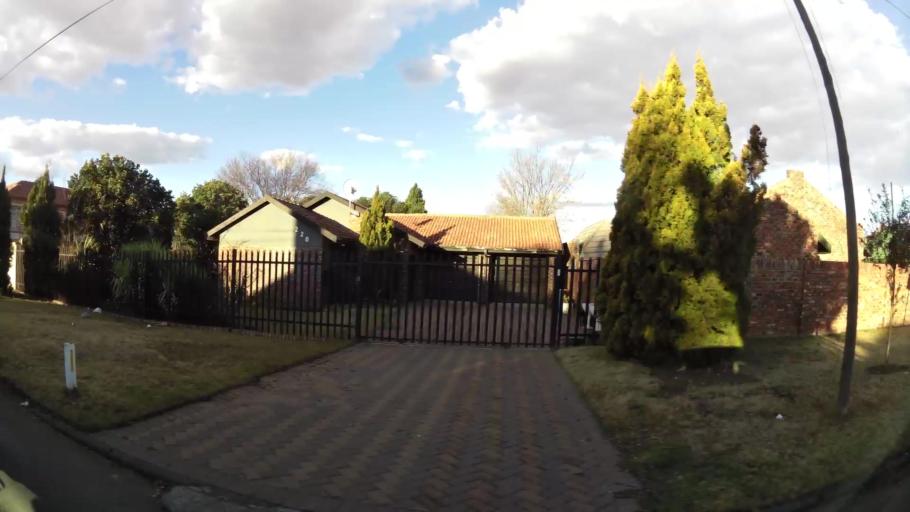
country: ZA
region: North-West
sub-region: Dr Kenneth Kaunda District Municipality
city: Potchefstroom
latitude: -26.7292
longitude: 27.0999
